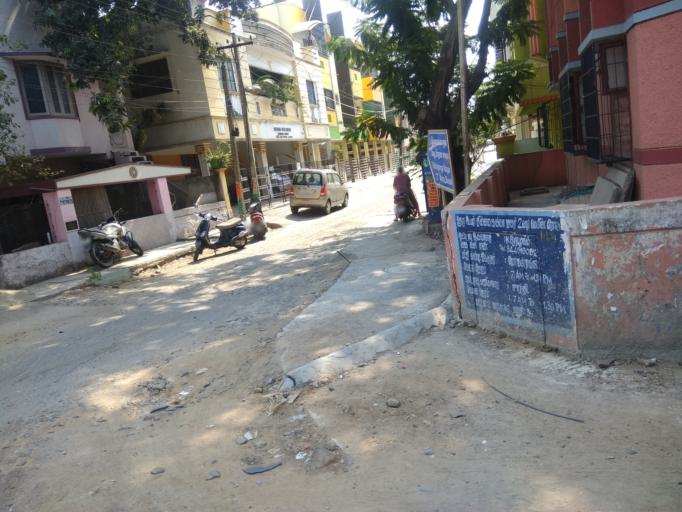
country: IN
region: Tamil Nadu
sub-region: Kancheepuram
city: Saint Thomas Mount
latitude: 12.9906
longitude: 80.1935
